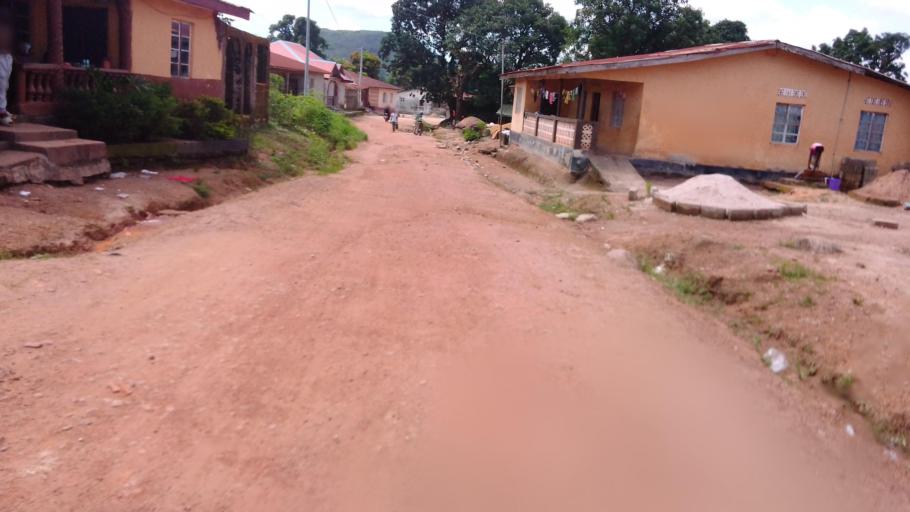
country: SL
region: Northern Province
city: Makeni
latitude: 8.8849
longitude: -12.0361
